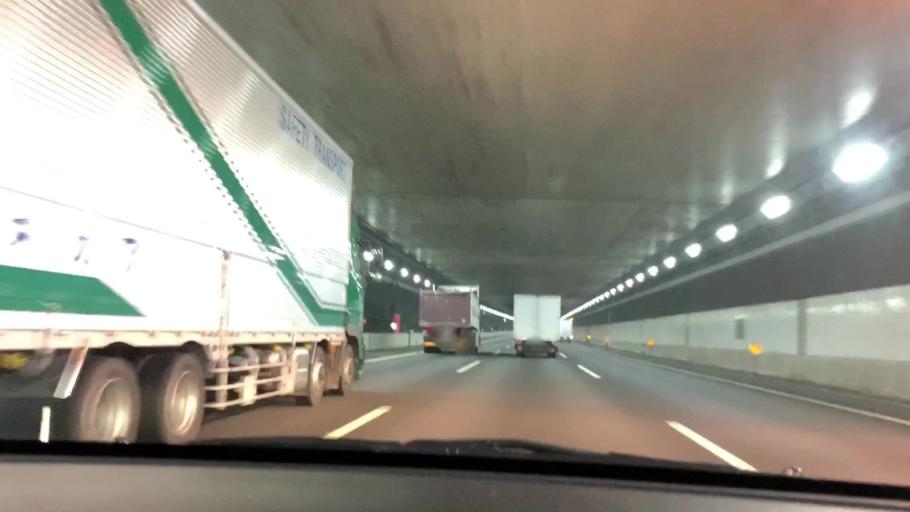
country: JP
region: Chiba
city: Nagareyama
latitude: 35.8926
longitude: 139.9169
